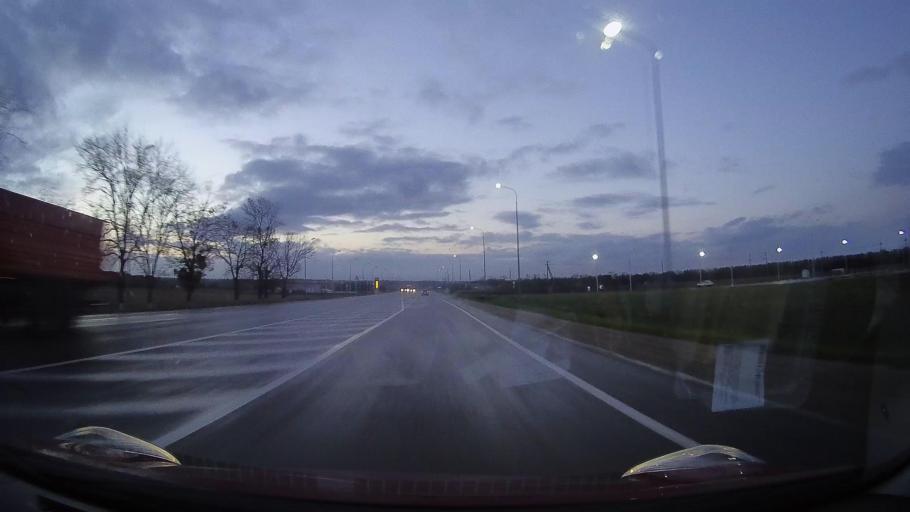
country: RU
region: Krasnodarskiy
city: Zavetnyy
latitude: 44.9086
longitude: 41.1684
